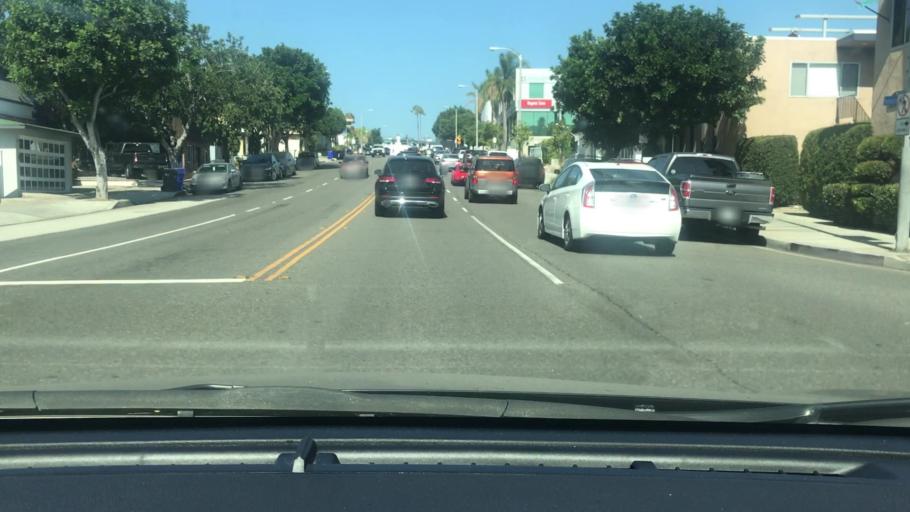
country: US
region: California
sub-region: Los Angeles County
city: Manhattan Beach
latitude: 33.8874
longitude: -118.4005
